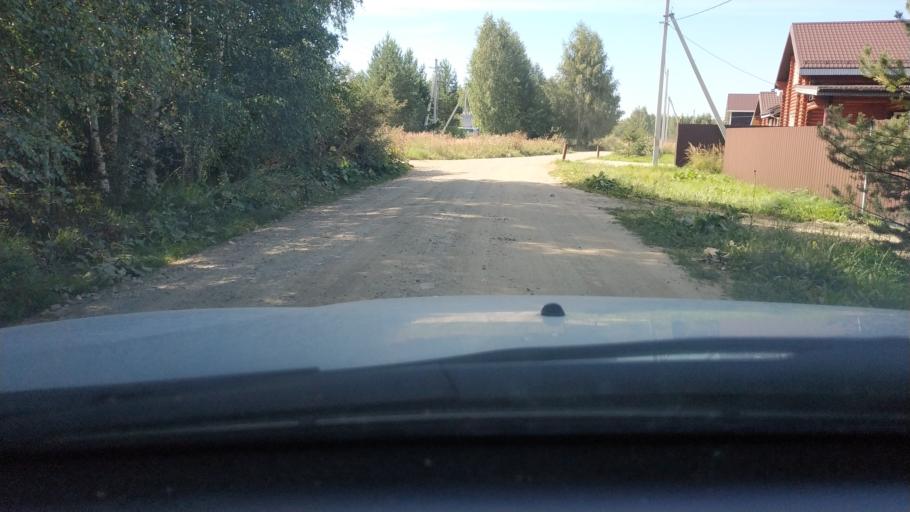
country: RU
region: Kostroma
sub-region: Kostromskoy Rayon
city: Kostroma
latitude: 57.7765
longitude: 40.7404
